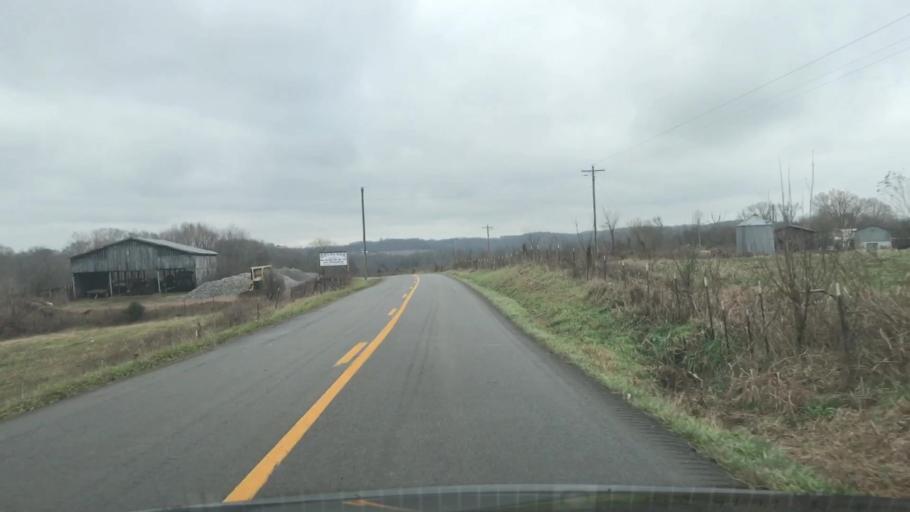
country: US
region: Kentucky
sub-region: Monroe County
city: Tompkinsville
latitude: 36.8258
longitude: -85.7494
